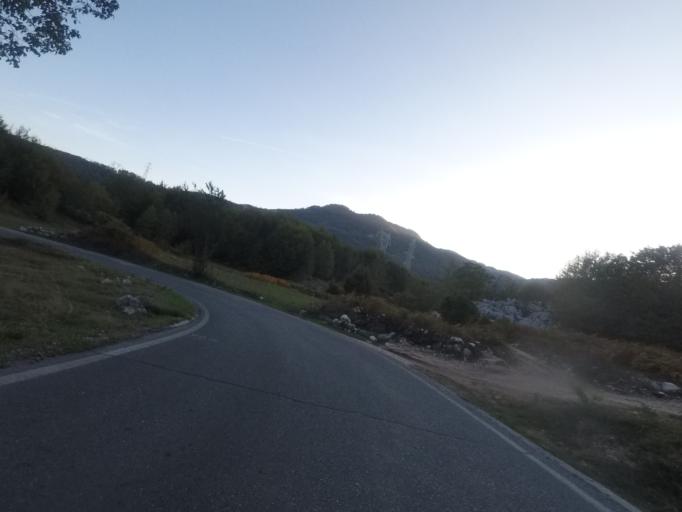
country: ME
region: Cetinje
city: Cetinje
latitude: 42.3668
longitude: 18.8866
